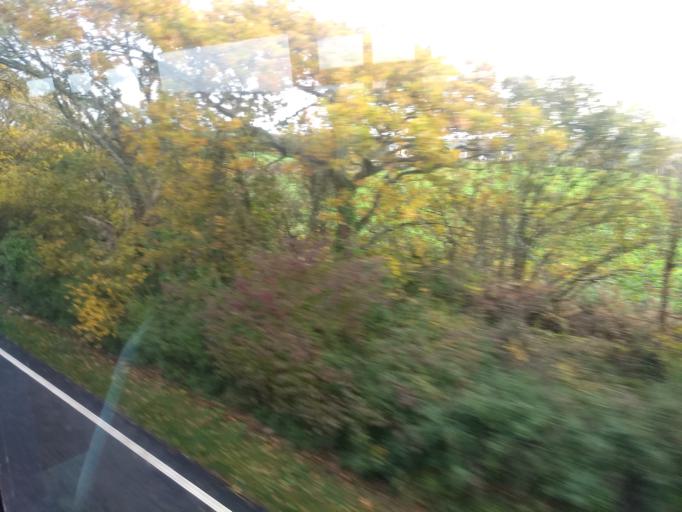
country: GB
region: England
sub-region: Isle of Wight
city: Shalfleet
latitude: 50.7028
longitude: -1.3622
